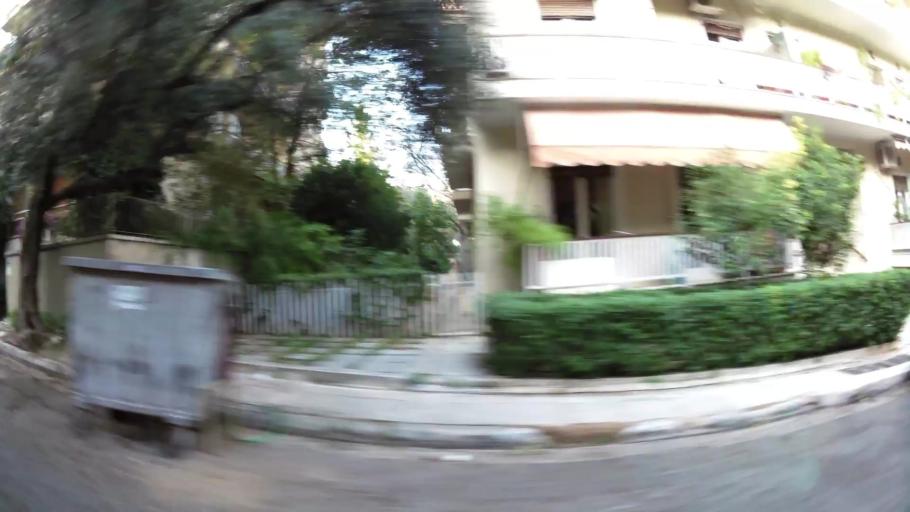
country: GR
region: Attica
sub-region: Nomarchia Athinas
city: Psychiko
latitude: 37.9978
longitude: 23.7669
